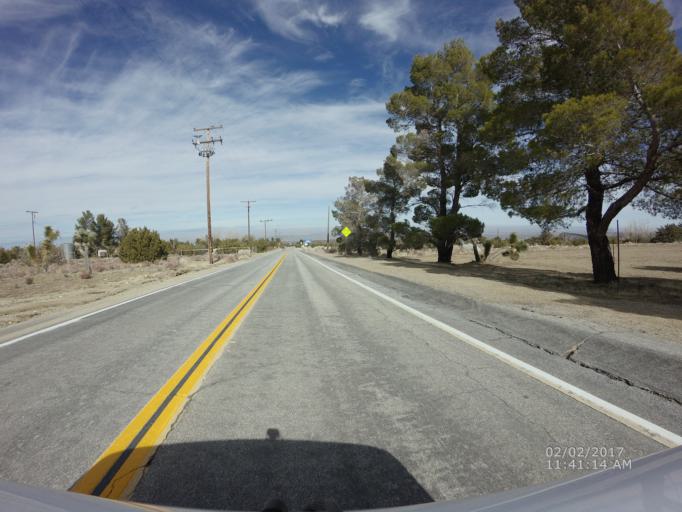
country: US
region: California
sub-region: Los Angeles County
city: Littlerock
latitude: 34.4449
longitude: -117.9359
